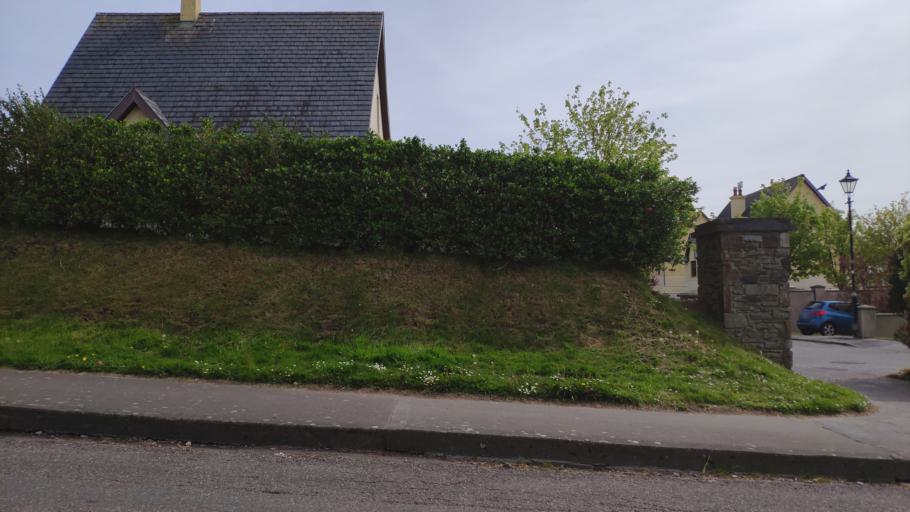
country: IE
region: Munster
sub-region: County Cork
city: Blarney
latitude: 51.9805
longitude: -8.5144
